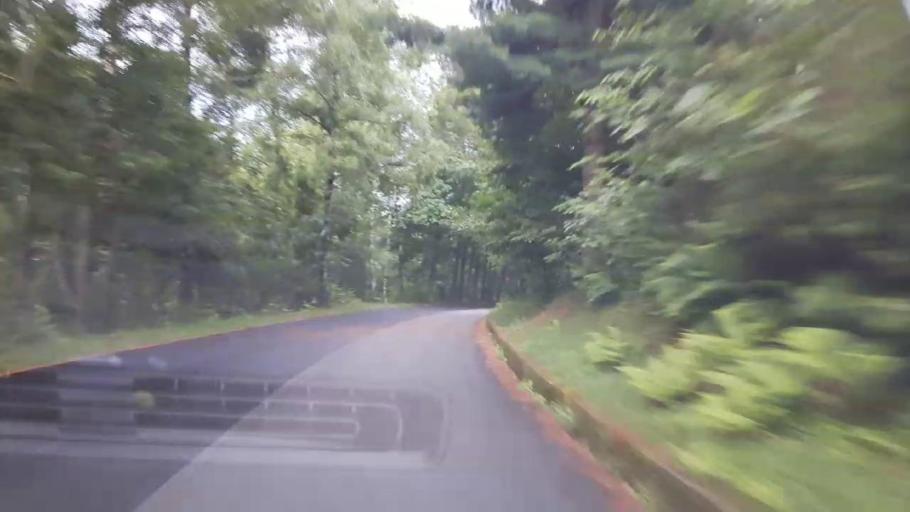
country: IT
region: Piedmont
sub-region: Provincia Verbano-Cusio-Ossola
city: Gignese
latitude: 45.8703
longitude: 8.4985
